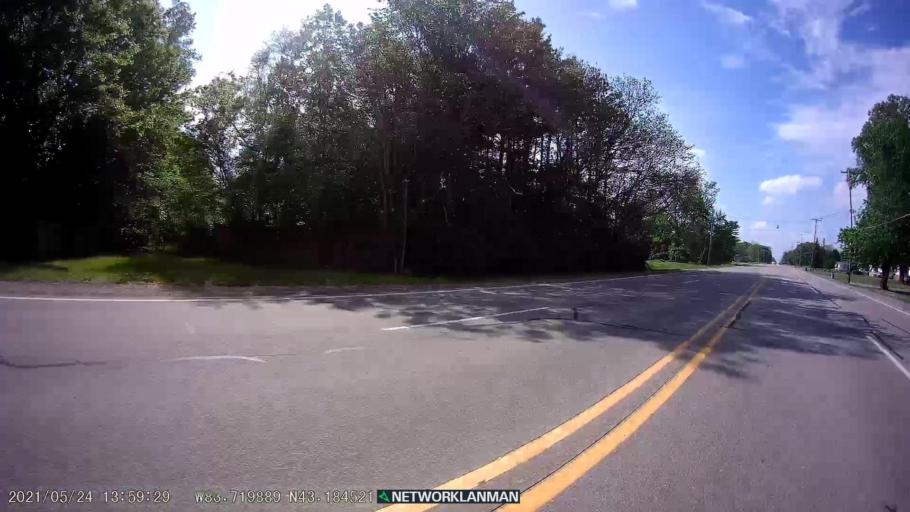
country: US
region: Michigan
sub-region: Genesee County
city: Clio
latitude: 43.1874
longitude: -83.7188
